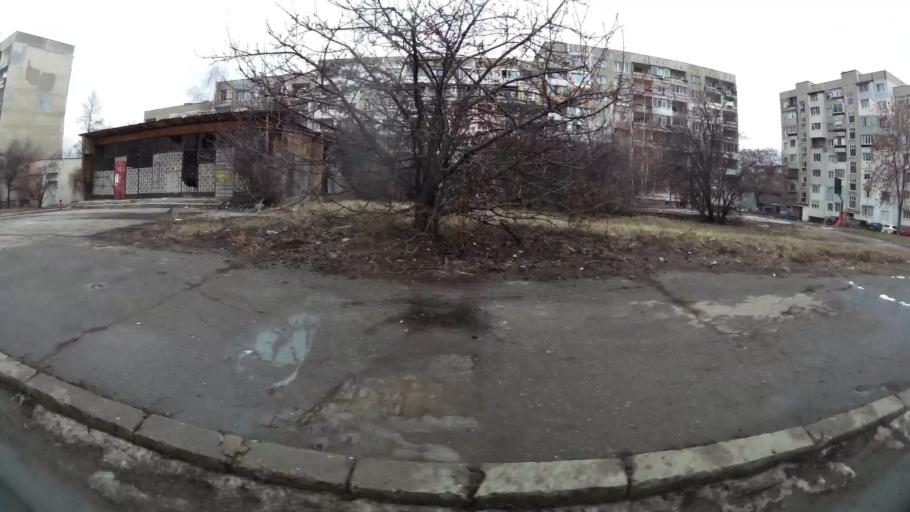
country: BG
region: Sofiya
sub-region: Obshtina Bozhurishte
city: Bozhurishte
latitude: 42.7241
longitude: 23.2555
